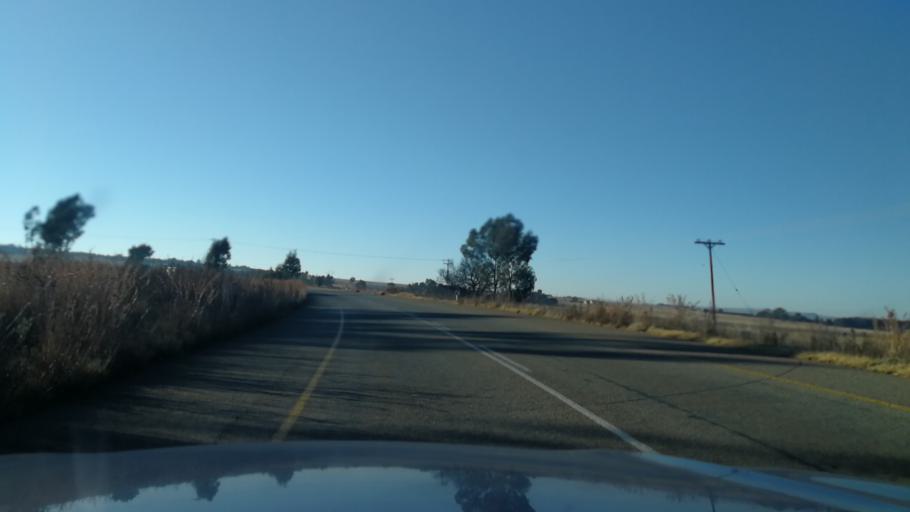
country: ZA
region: North-West
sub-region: Bojanala Platinum District Municipality
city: Koster
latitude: -25.9307
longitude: 27.1269
